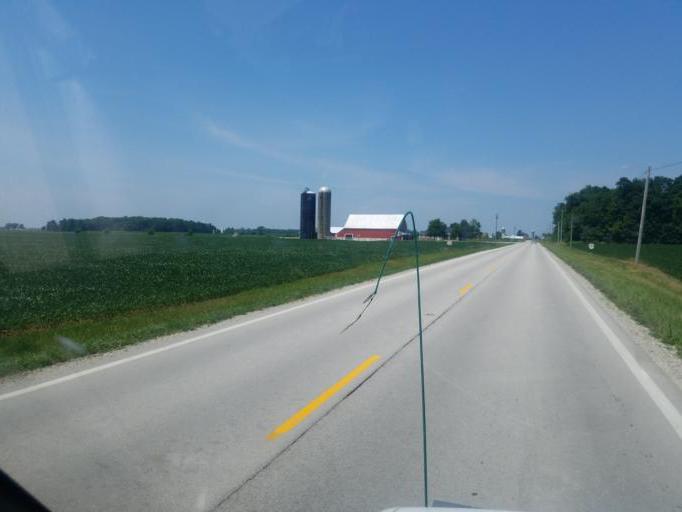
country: US
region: Ohio
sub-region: Shelby County
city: Fort Loramie
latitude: 40.3441
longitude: -84.4346
